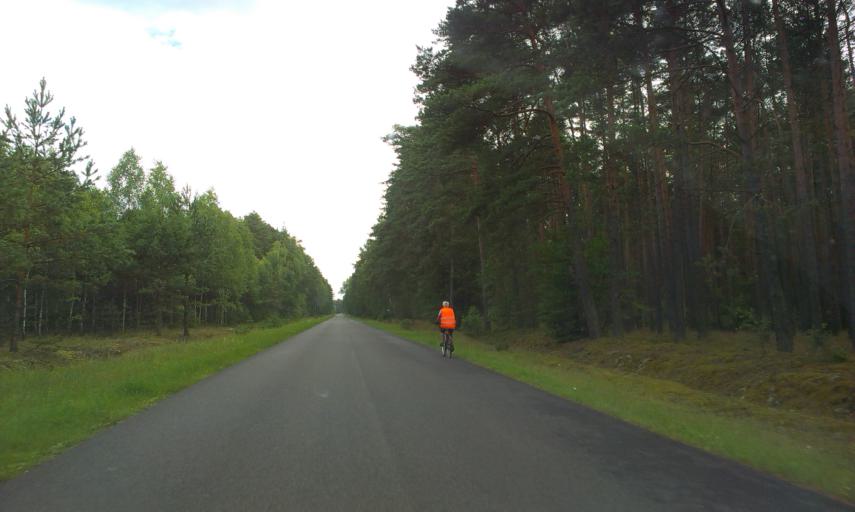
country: PL
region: Greater Poland Voivodeship
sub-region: Powiat zlotowski
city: Okonek
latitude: 53.5228
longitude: 16.9652
